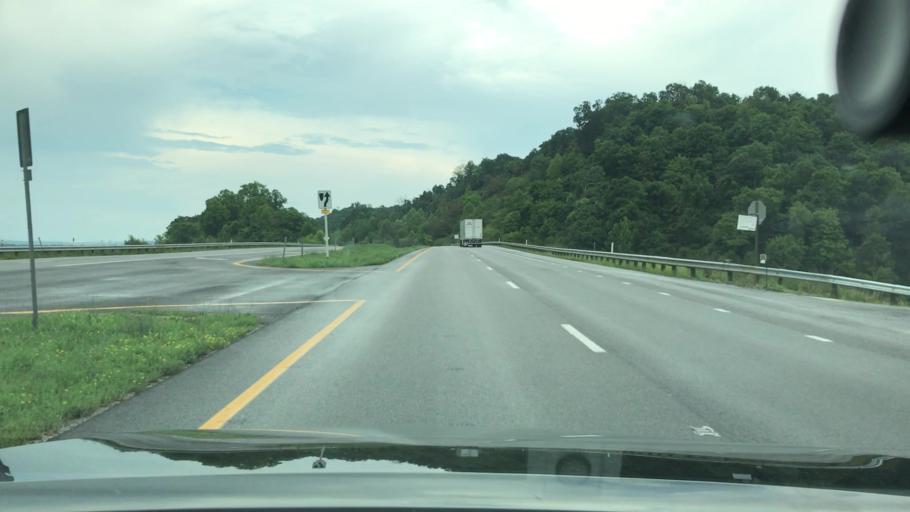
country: US
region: West Virginia
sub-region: Mason County
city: Point Pleasant
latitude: 38.8243
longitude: -82.1269
